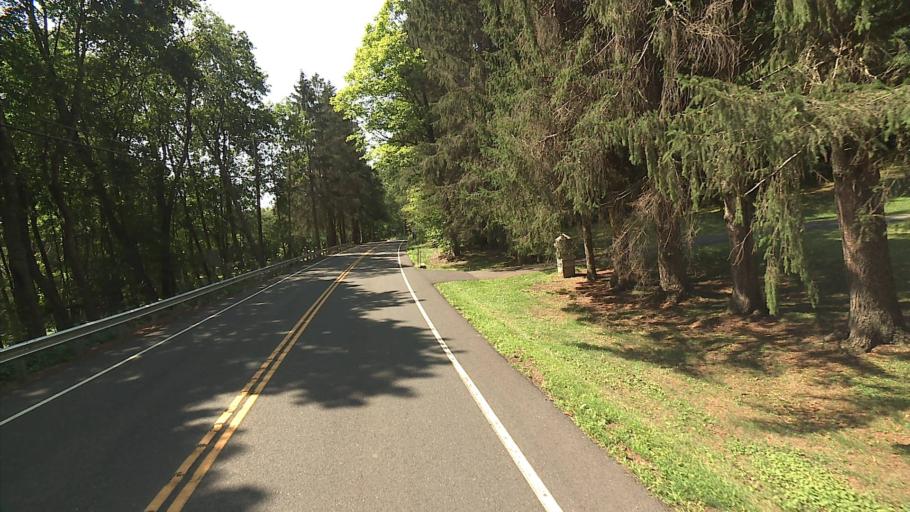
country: US
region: Massachusetts
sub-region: Berkshire County
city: New Marlborough
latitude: 42.0059
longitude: -73.2038
